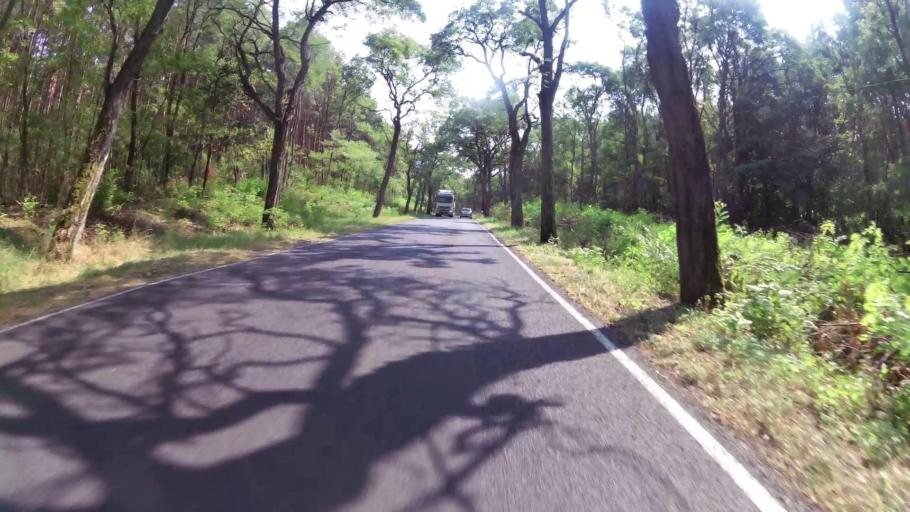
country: PL
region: West Pomeranian Voivodeship
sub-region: Powiat gryfinski
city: Moryn
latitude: 52.8326
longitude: 14.4150
